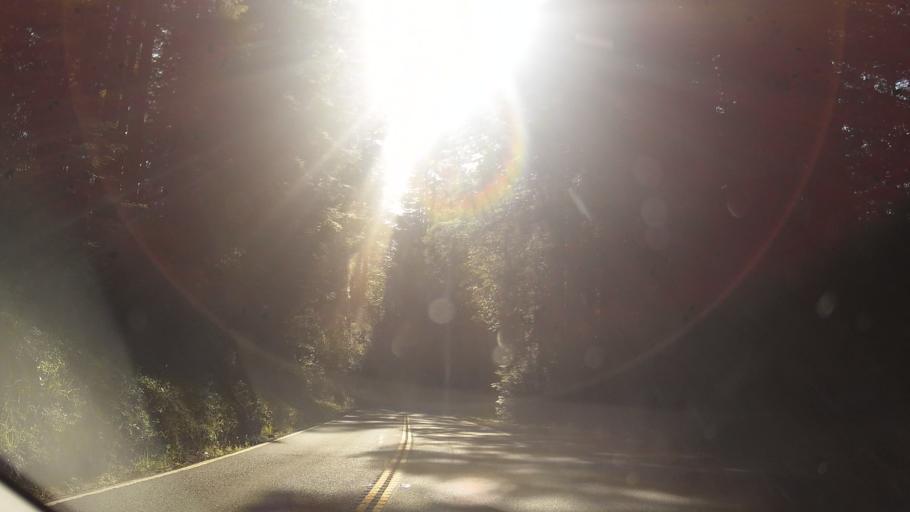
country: US
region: California
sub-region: Mendocino County
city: Fort Bragg
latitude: 39.3771
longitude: -123.6873
